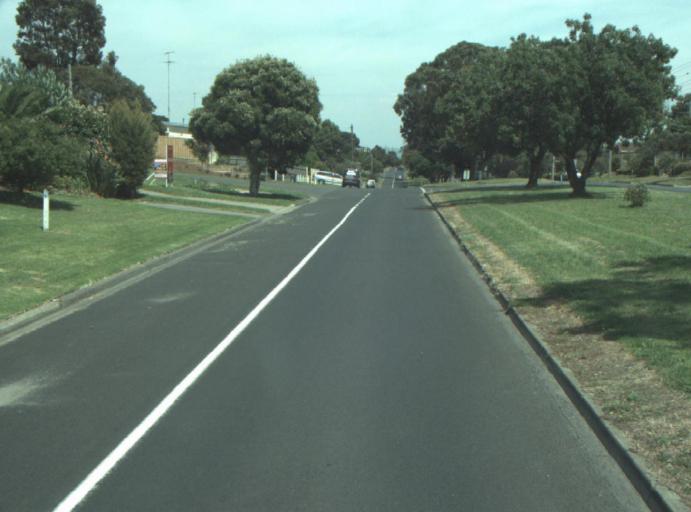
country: AU
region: Victoria
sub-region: Greater Geelong
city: Clifton Springs
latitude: -38.1587
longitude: 144.5714
